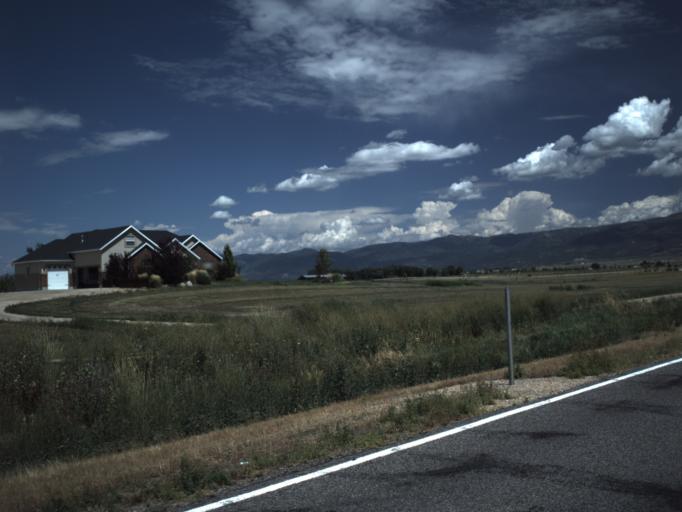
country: US
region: Utah
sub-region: Sanpete County
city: Moroni
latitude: 39.4809
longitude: -111.5310
